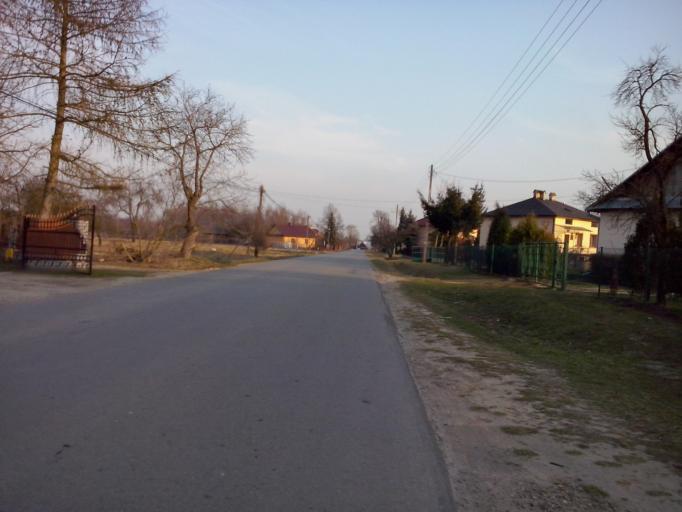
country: PL
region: Subcarpathian Voivodeship
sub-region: Powiat nizanski
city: Krzeszow
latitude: 50.3988
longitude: 22.3548
